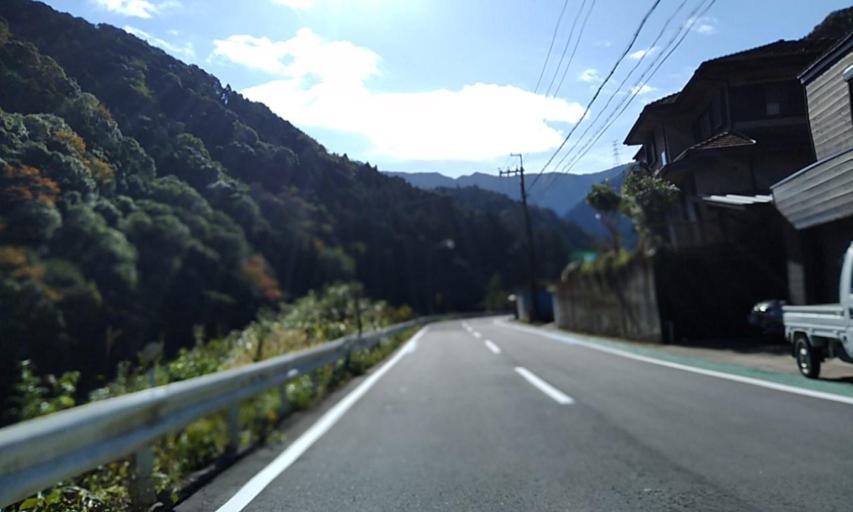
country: JP
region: Wakayama
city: Kainan
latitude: 34.0546
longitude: 135.3555
